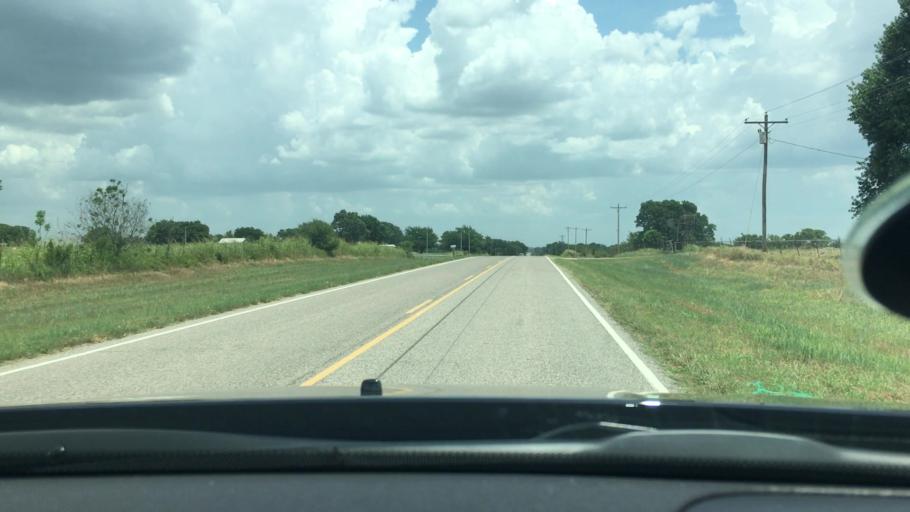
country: US
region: Oklahoma
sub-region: Love County
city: Marietta
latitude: 33.9839
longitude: -96.9607
